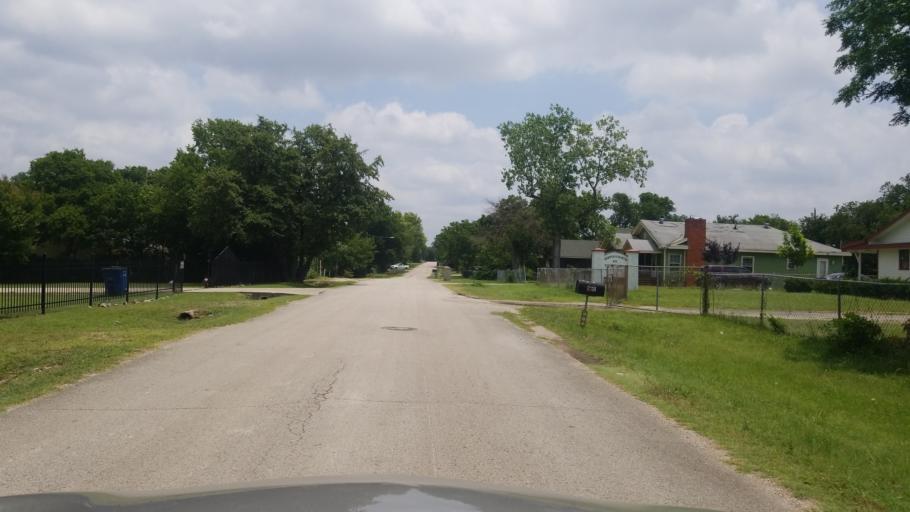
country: US
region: Texas
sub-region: Dallas County
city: Duncanville
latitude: 32.6931
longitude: -96.9271
